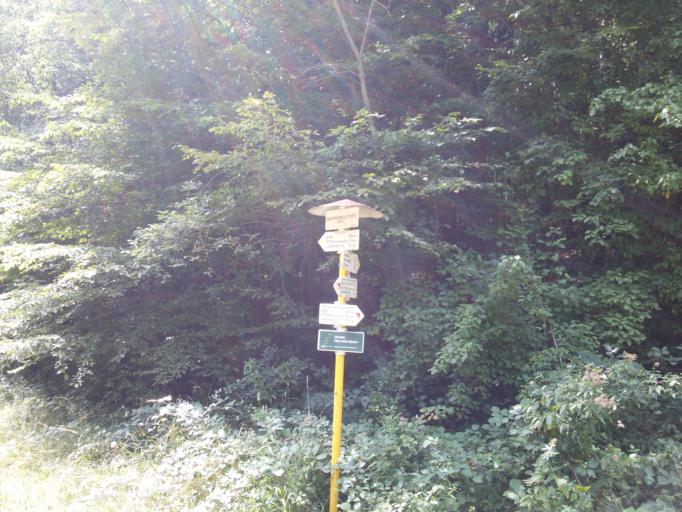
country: CZ
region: Zlin
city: Pozlovice
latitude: 49.1158
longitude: 17.7608
